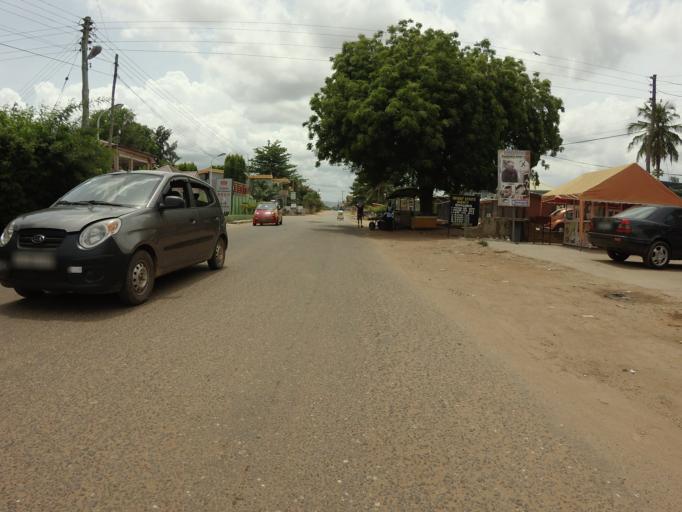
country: GH
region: Greater Accra
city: Dome
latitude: 5.6246
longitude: -0.2424
